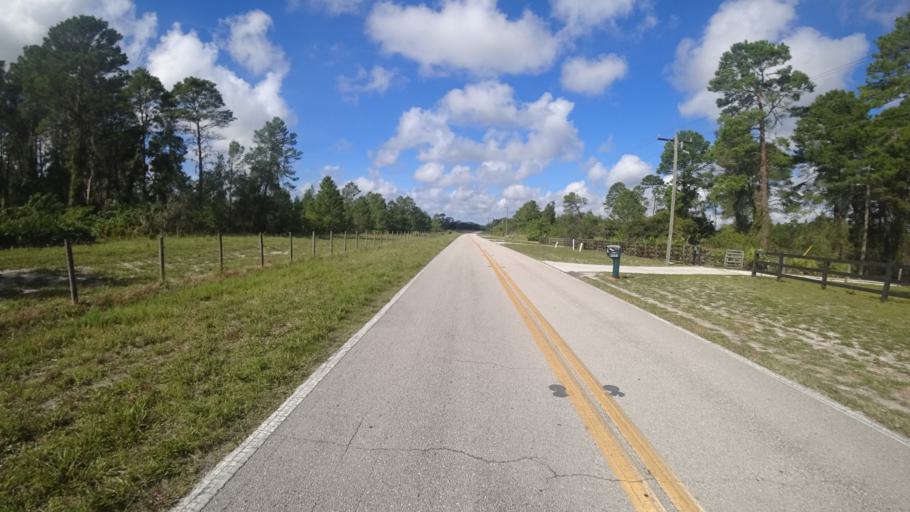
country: US
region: Florida
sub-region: Sarasota County
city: Lake Sarasota
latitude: 27.3391
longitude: -82.1928
